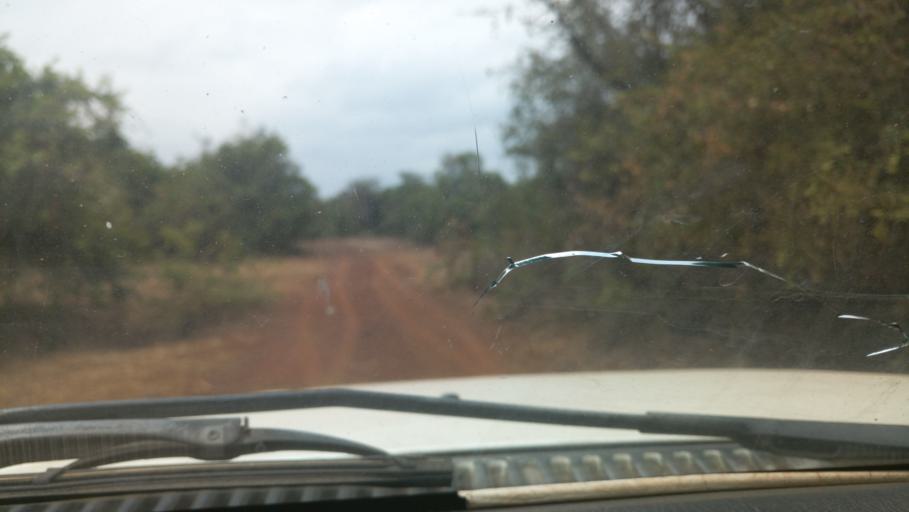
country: KE
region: Nairobi Area
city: Nairobi
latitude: -1.3499
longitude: 36.7673
